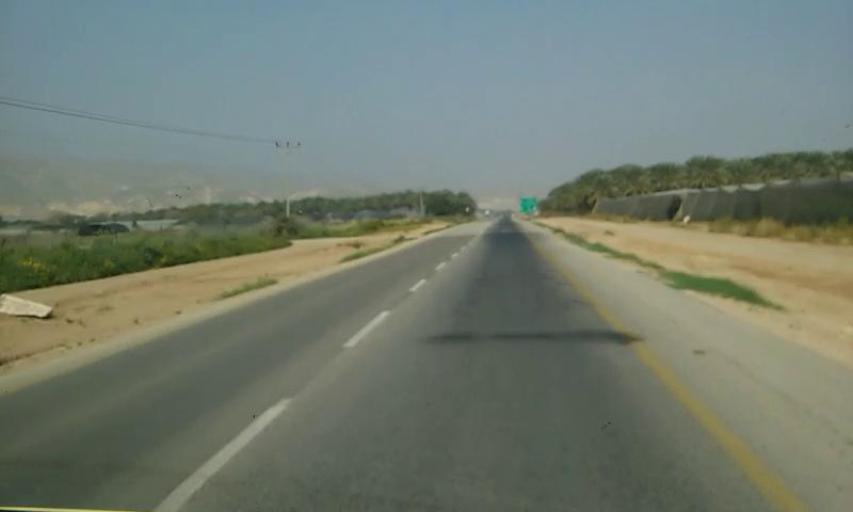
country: PS
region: West Bank
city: Al Fasayil
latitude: 31.9966
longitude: 35.4559
